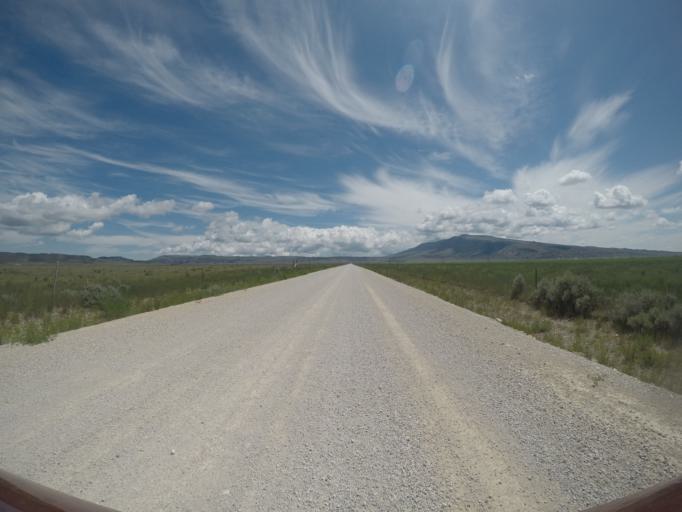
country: US
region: Montana
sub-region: Yellowstone County
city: Laurel
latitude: 45.2196
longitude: -108.7172
